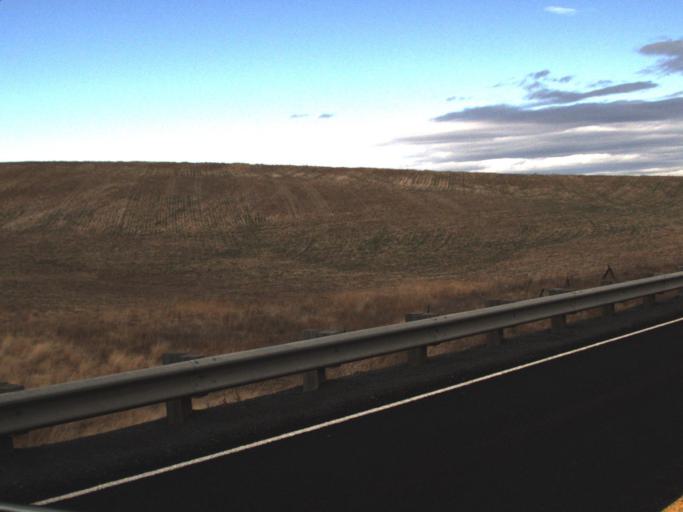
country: US
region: Washington
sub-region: Okanogan County
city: Coulee Dam
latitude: 47.8980
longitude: -118.8615
